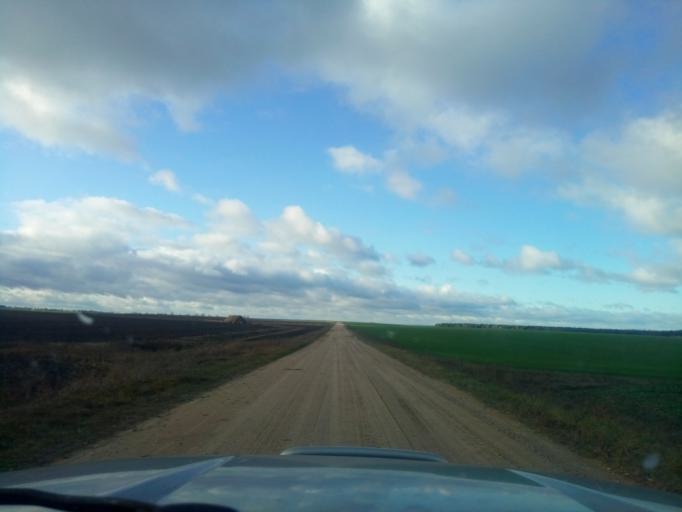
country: BY
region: Minsk
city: Tsimkavichy
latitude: 53.1966
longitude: 26.9234
